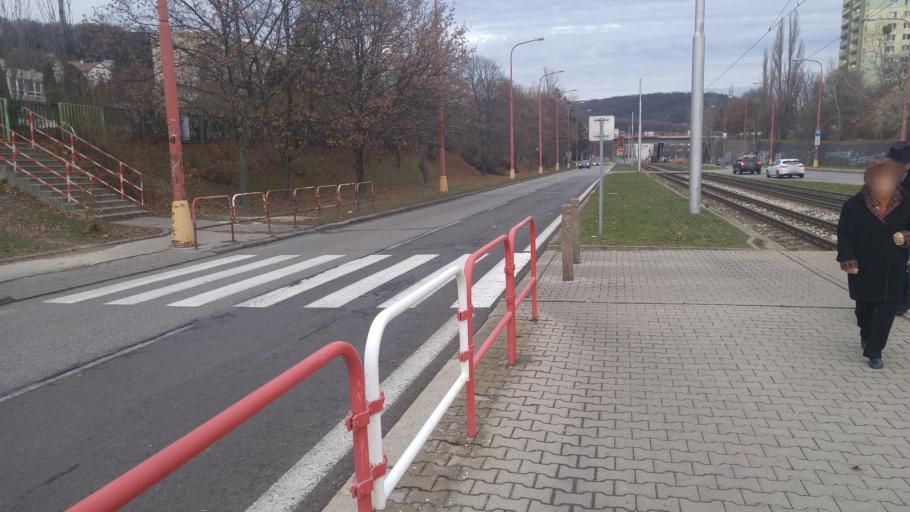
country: AT
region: Lower Austria
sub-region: Politischer Bezirk Bruck an der Leitha
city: Wolfsthal
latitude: 48.1628
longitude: 17.0481
